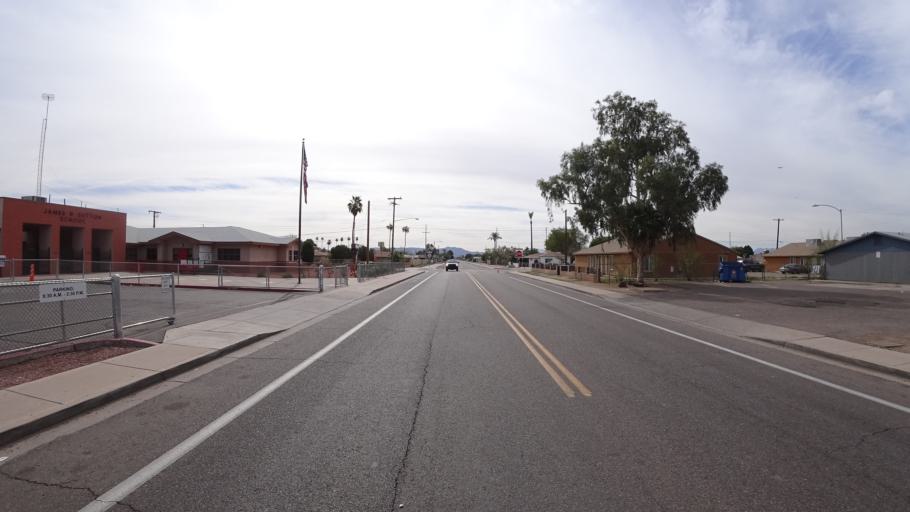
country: US
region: Arizona
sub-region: Maricopa County
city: Phoenix
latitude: 33.4593
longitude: -112.1259
